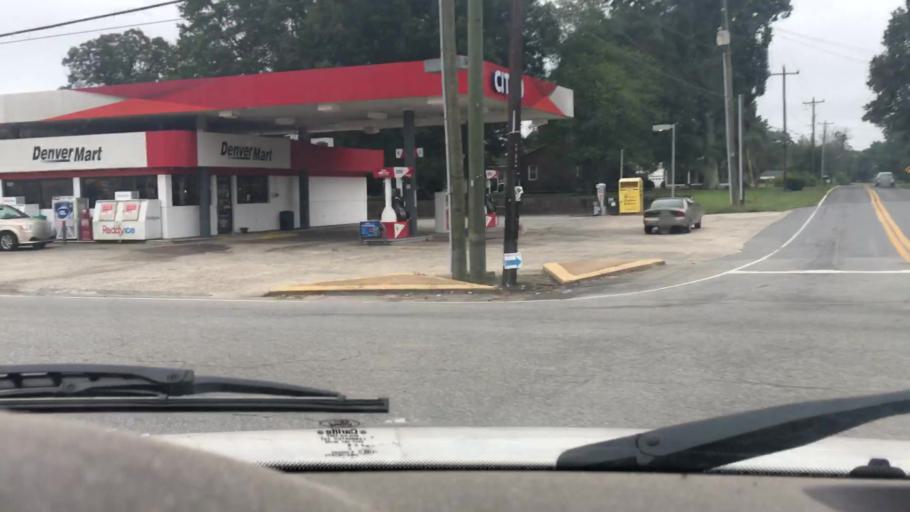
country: US
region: North Carolina
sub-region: Lincoln County
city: Denver
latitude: 35.5320
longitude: -81.0304
